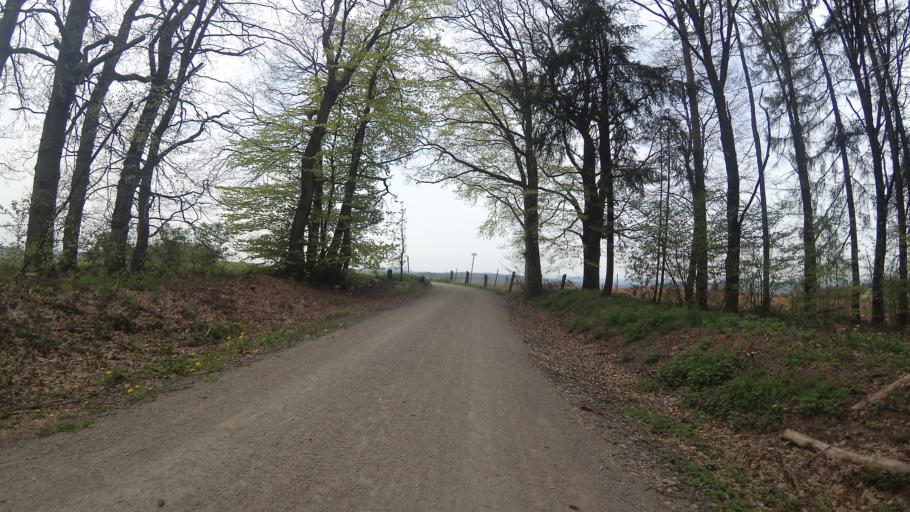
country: DE
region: Saarland
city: Mainzweiler
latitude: 49.4044
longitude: 7.1195
